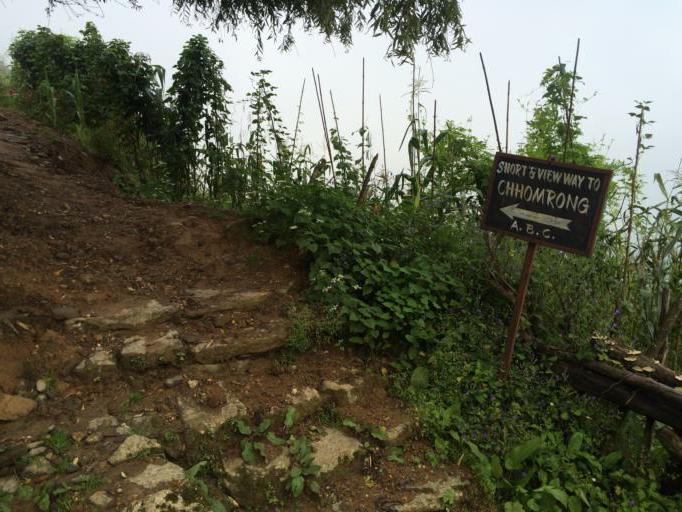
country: NP
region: Western Region
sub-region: Dhawalagiri Zone
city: Chitre
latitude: 28.4175
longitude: 83.8137
